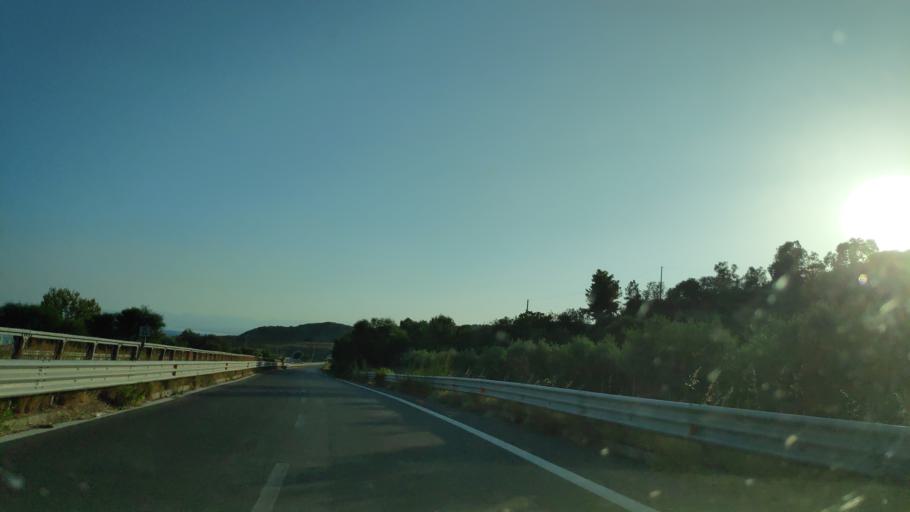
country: IT
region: Calabria
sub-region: Provincia di Reggio Calabria
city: Roccella Ionica
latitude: 38.3286
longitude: 16.3960
